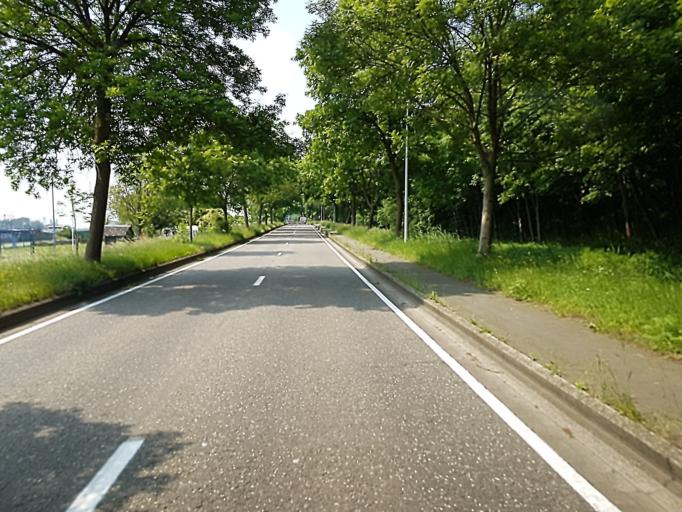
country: BE
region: Flanders
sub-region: Provincie Antwerpen
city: Schoten
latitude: 51.2379
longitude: 4.5054
